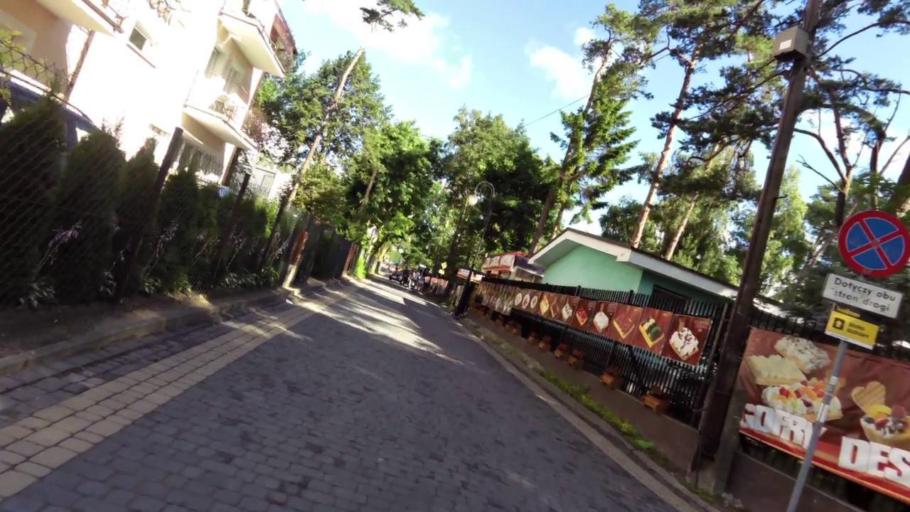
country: PL
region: West Pomeranian Voivodeship
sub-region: Powiat koszalinski
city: Mielno
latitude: 54.2627
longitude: 16.0631
